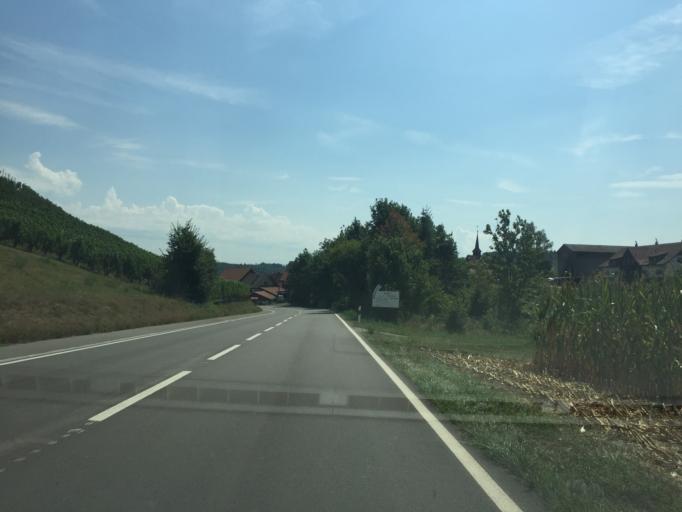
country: CH
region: Thurgau
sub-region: Frauenfeld District
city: Diessenhofen
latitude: 47.6233
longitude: 8.7750
